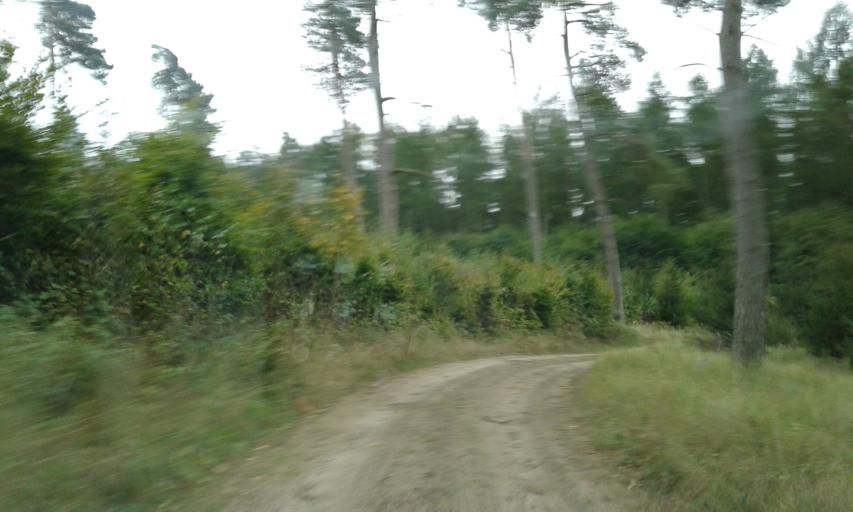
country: PL
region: West Pomeranian Voivodeship
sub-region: Powiat choszczenski
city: Pelczyce
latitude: 53.0856
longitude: 15.2524
